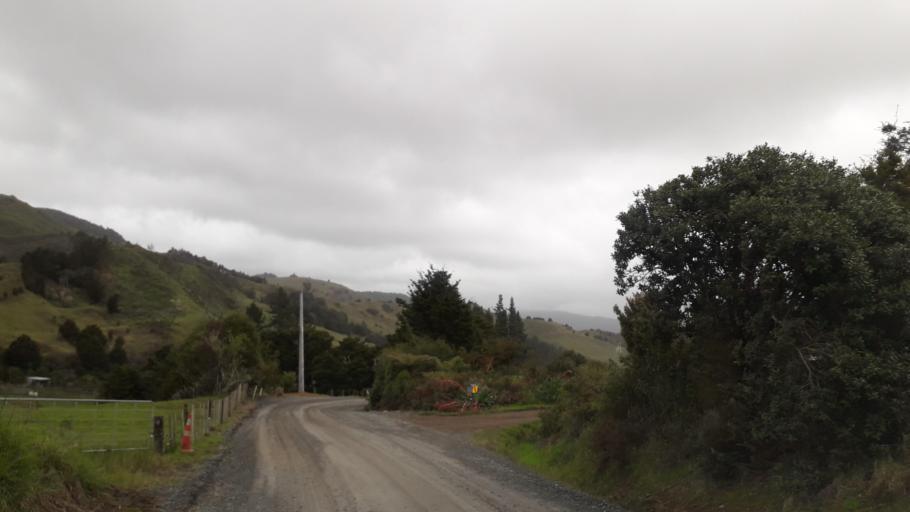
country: NZ
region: Northland
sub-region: Far North District
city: Kerikeri
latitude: -35.1261
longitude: 173.7448
